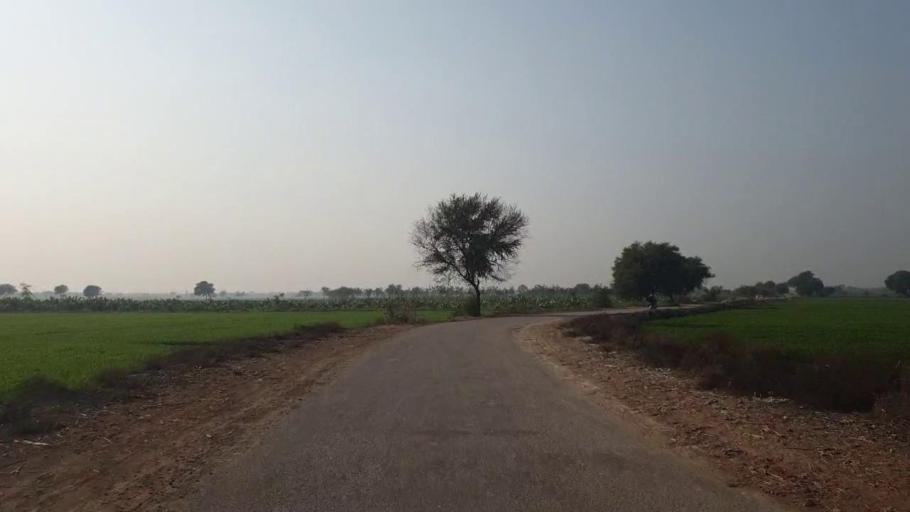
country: PK
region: Sindh
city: Shahdadpur
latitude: 25.9671
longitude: 68.5551
